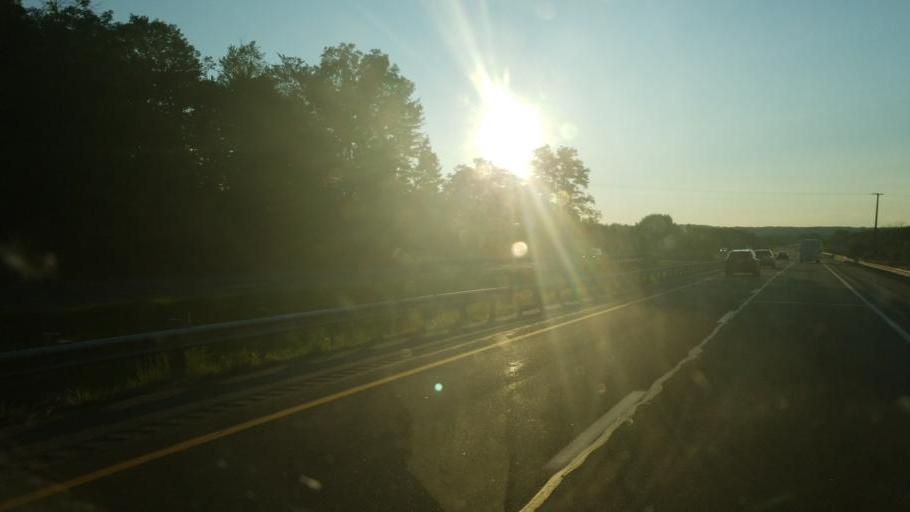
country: US
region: Ohio
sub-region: Mahoning County
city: Boardman
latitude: 40.9743
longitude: -80.6675
